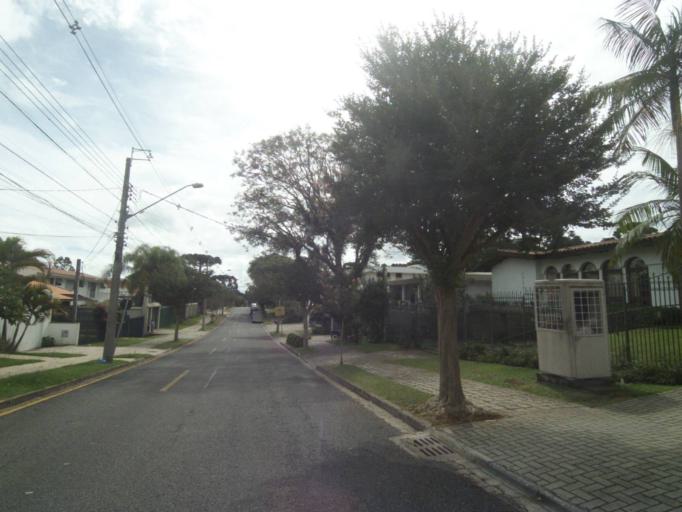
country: BR
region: Parana
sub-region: Curitiba
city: Curitiba
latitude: -25.4438
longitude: -49.2978
